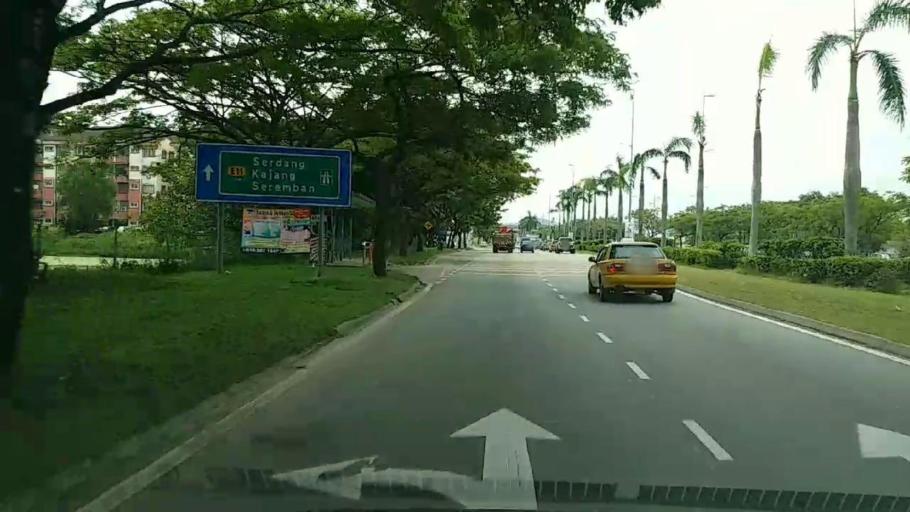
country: MY
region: Putrajaya
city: Putrajaya
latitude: 2.9464
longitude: 101.6169
